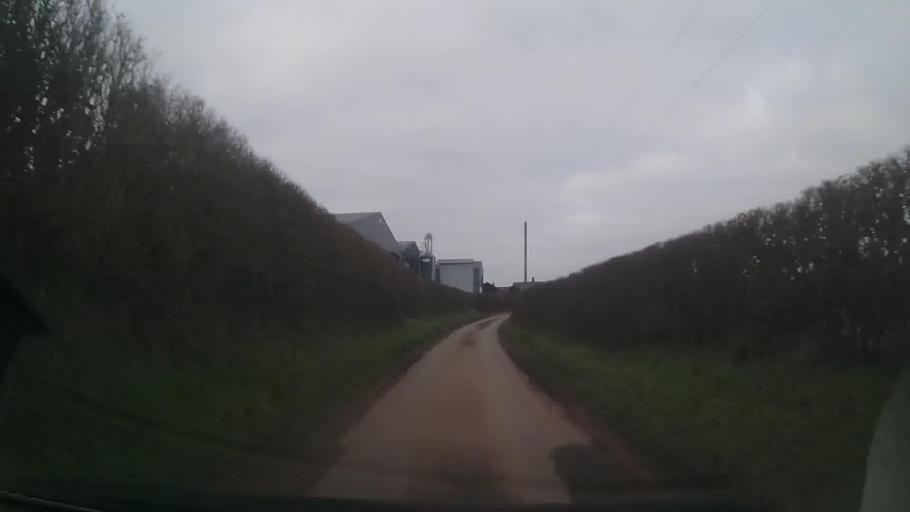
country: GB
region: England
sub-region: Shropshire
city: Petton
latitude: 52.7987
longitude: -2.8183
